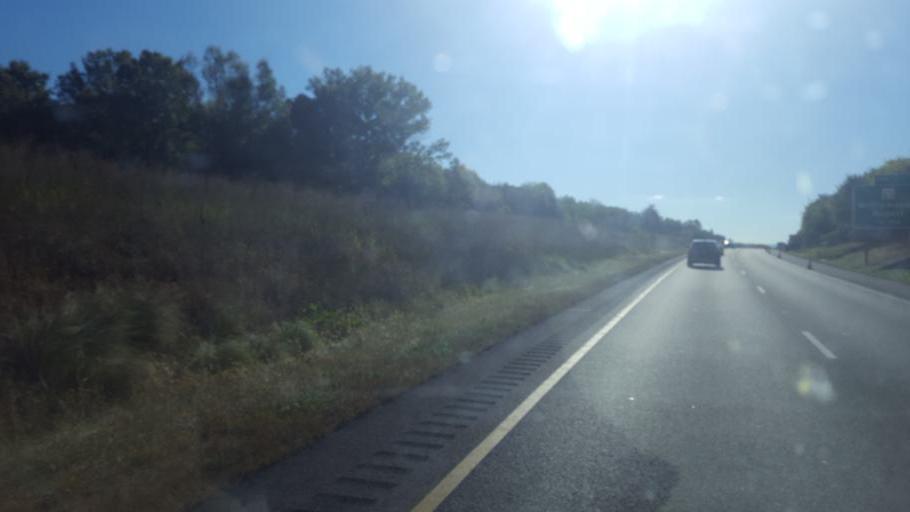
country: US
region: Maryland
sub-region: Washington County
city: Wilson-Conococheague
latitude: 39.6359
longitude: -77.8187
